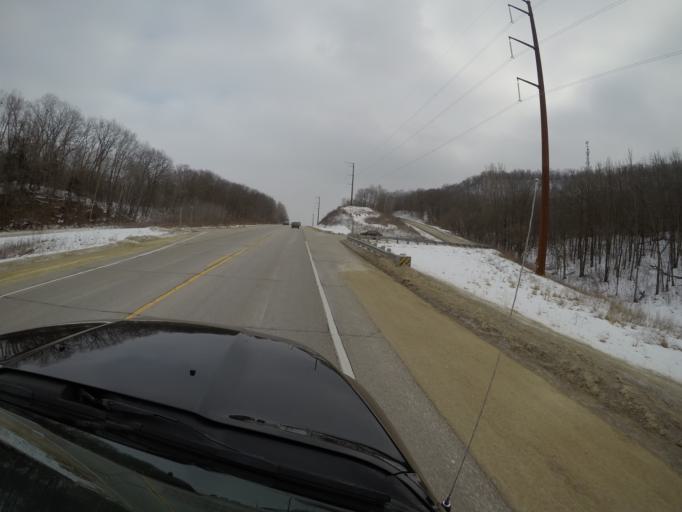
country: US
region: Wisconsin
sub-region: Trempealeau County
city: Galesville
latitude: 44.0725
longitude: -91.3277
